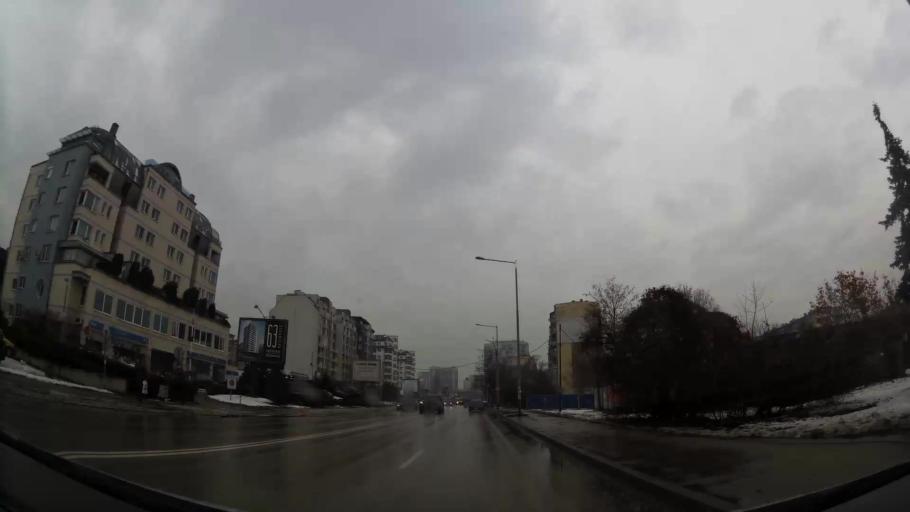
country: BG
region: Sofia-Capital
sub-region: Stolichna Obshtina
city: Sofia
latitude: 42.6666
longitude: 23.2842
